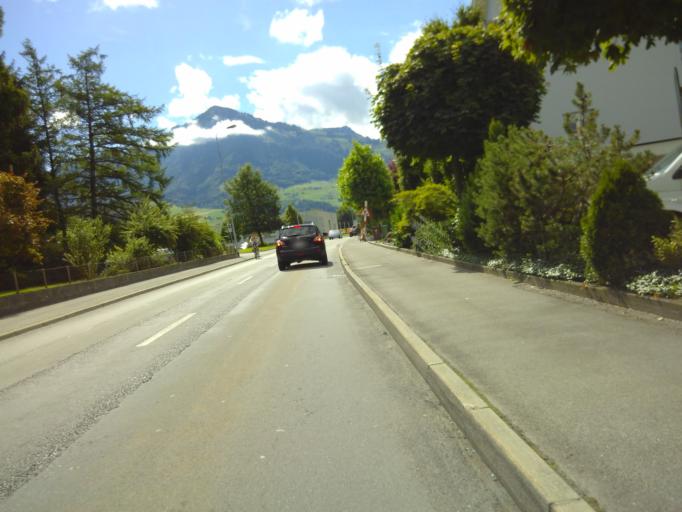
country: CH
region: Nidwalden
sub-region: Nidwalden
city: Stans
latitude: 46.9618
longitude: 8.3615
